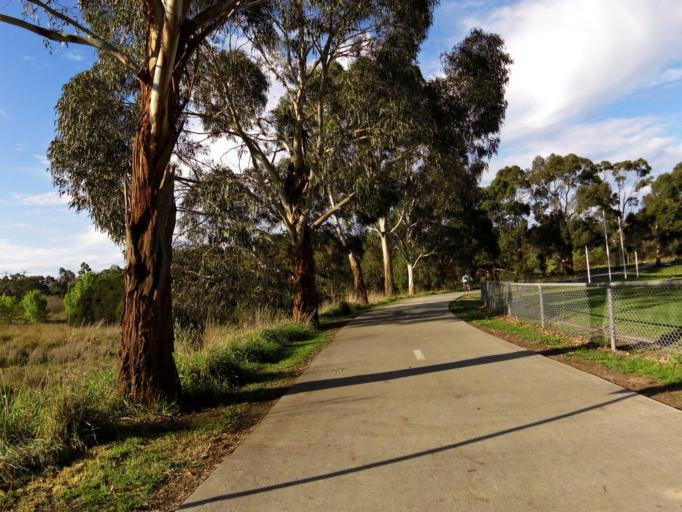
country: AU
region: Victoria
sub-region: Knox
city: Wantirna
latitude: -37.8561
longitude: 145.2101
